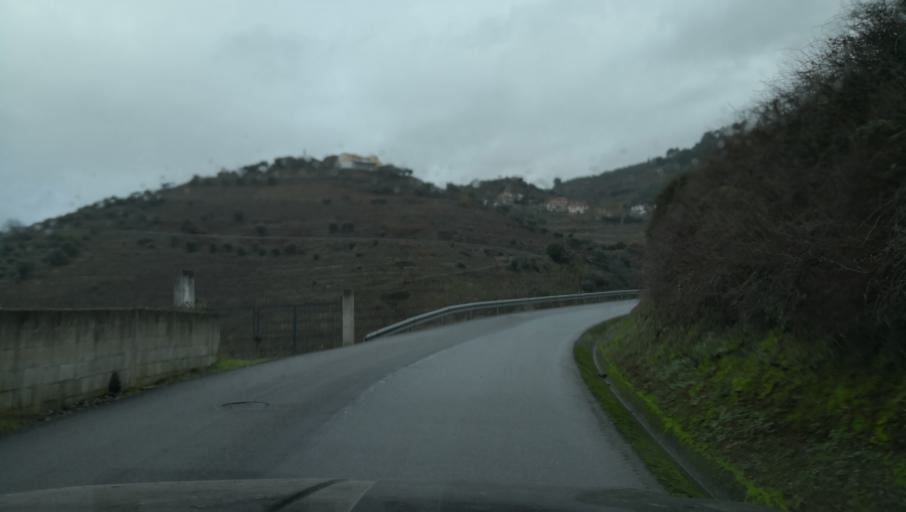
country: PT
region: Vila Real
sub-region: Santa Marta de Penaguiao
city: Santa Marta de Penaguiao
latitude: 41.2008
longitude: -7.7511
